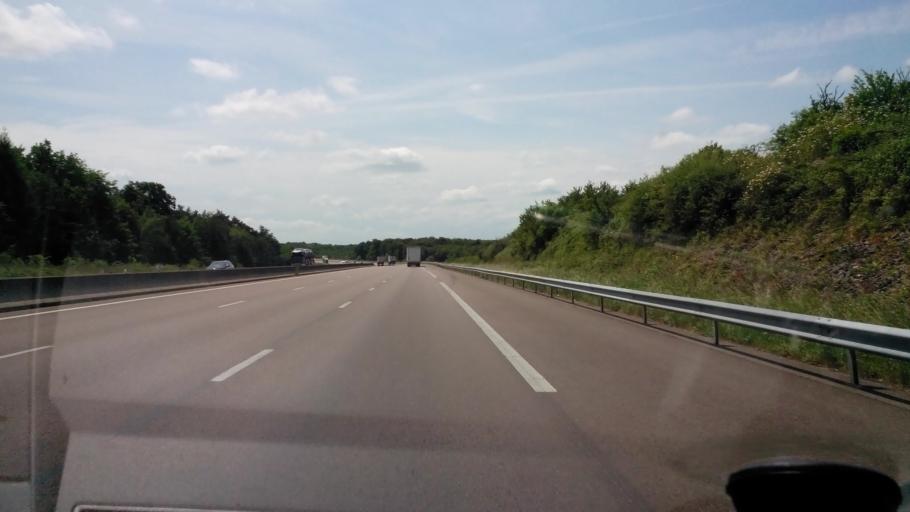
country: FR
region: Bourgogne
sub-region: Departement de la Cote-d'Or
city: Selongey
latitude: 47.6282
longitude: 5.1792
